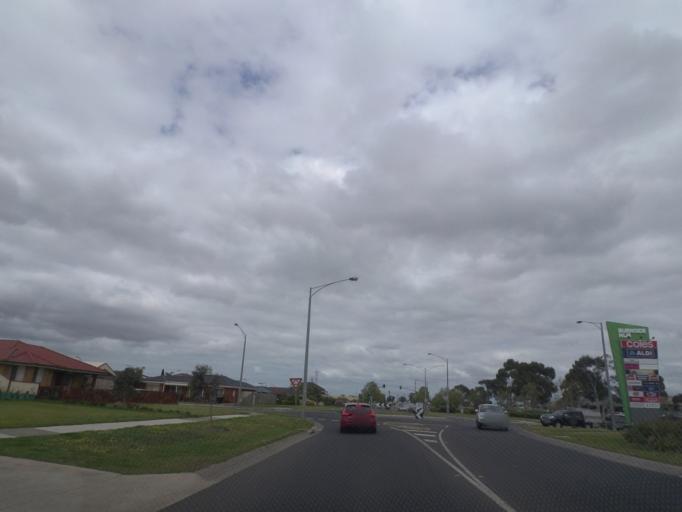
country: AU
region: Victoria
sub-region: Melton
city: Caroline Springs
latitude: -37.7583
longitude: 144.7555
